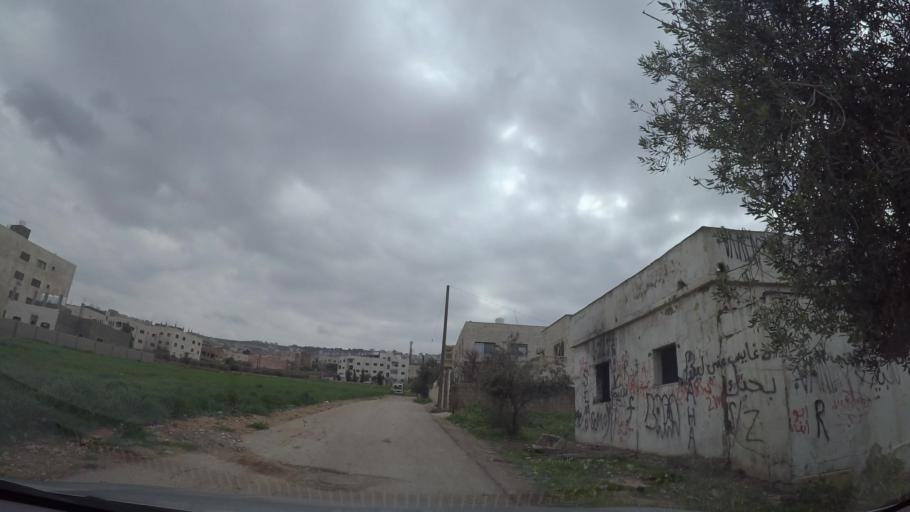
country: JO
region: Amman
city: Al Jubayhah
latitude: 32.0535
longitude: 35.8419
